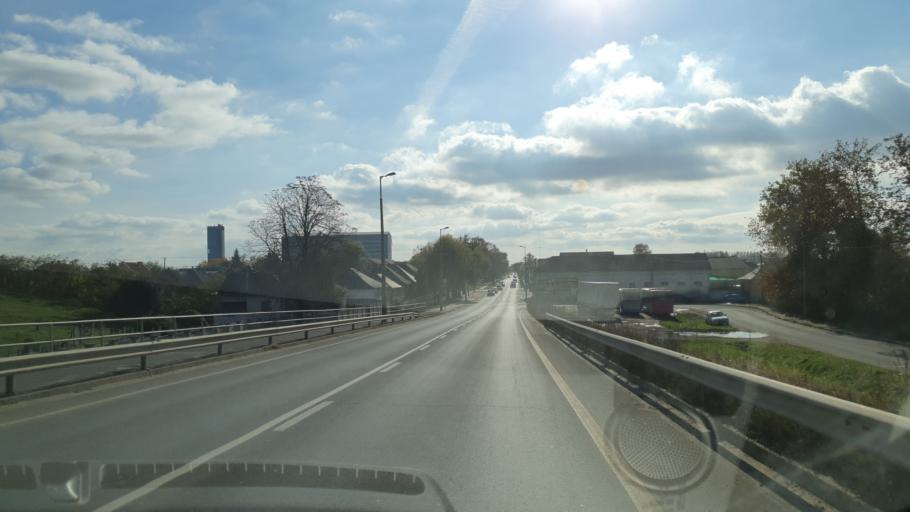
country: HU
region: Szabolcs-Szatmar-Bereg
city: Kisvarda
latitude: 48.2121
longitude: 22.0856
